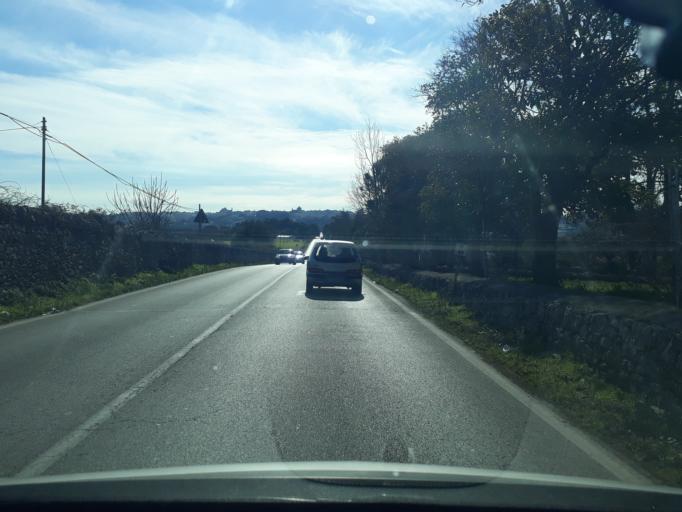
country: IT
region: Apulia
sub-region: Provincia di Taranto
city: Martina Franca
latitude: 40.7294
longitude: 17.3326
